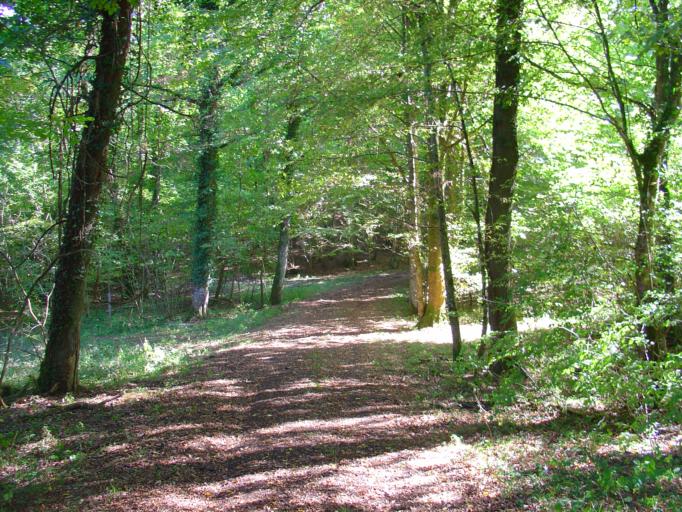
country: FR
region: Lorraine
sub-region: Departement de Meurthe-et-Moselle
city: Saizerais
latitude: 48.8239
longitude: 5.9631
